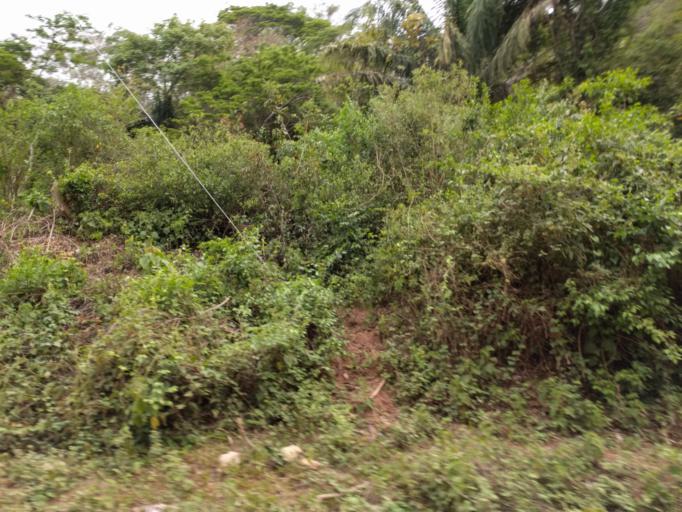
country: BO
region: Santa Cruz
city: Santiago del Torno
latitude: -17.9153
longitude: -63.4305
